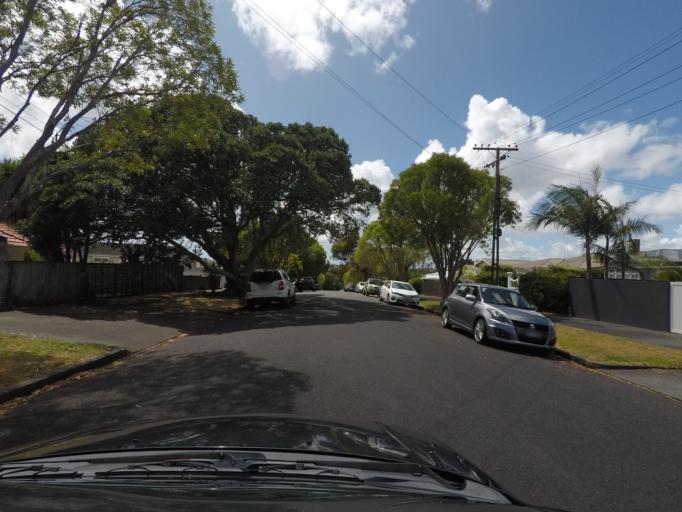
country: NZ
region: Auckland
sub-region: Auckland
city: Rosebank
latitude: -36.8589
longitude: 174.7062
